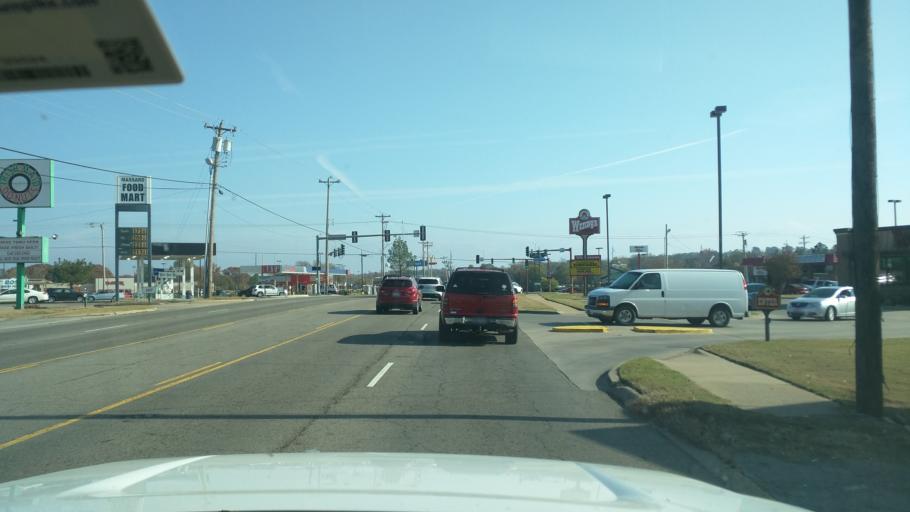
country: US
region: Arkansas
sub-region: Sebastian County
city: Barling
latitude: 35.3487
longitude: -94.3417
